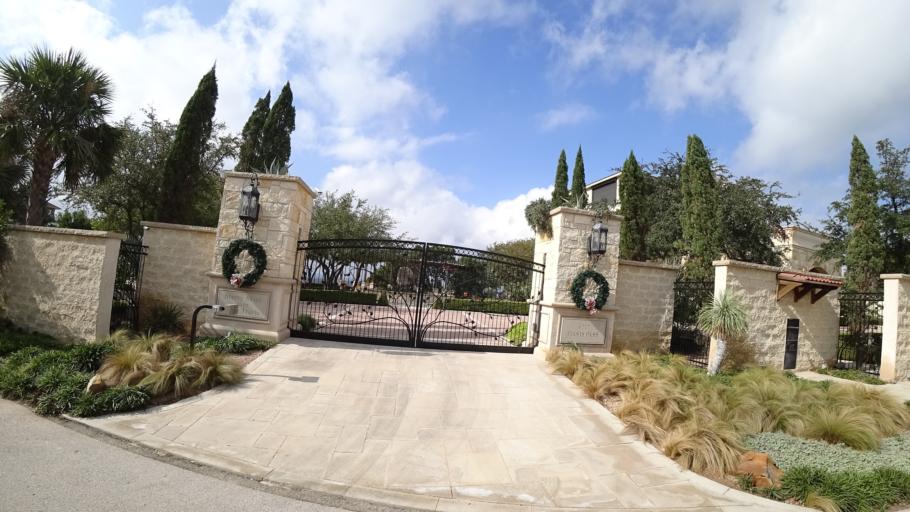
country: US
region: Texas
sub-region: Travis County
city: Hudson Bend
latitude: 30.4111
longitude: -97.8750
